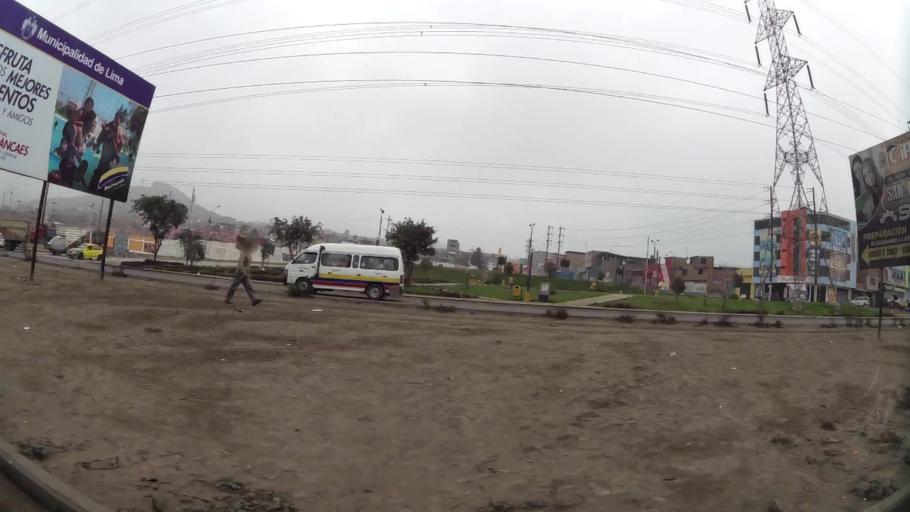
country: PE
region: Lima
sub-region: Lima
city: Surco
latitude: -12.1930
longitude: -76.9350
